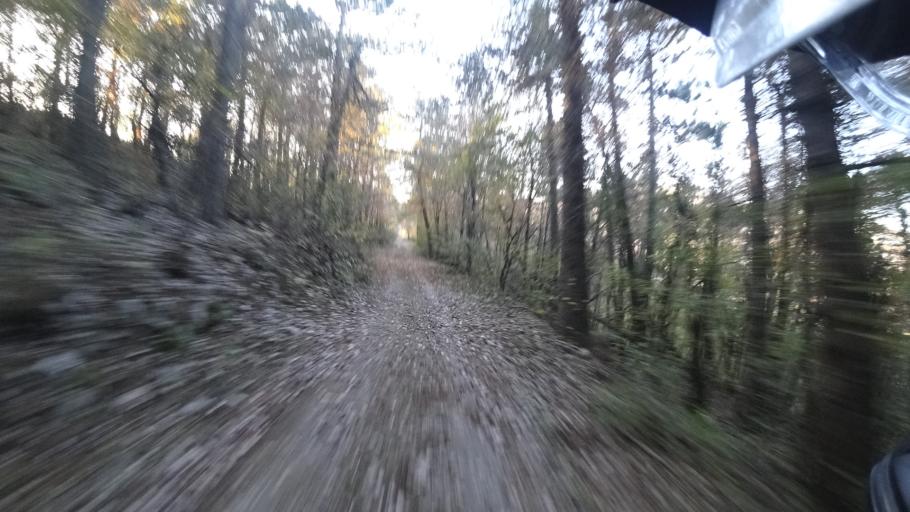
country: HR
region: Primorsko-Goranska
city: Klana
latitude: 45.4958
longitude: 14.4104
